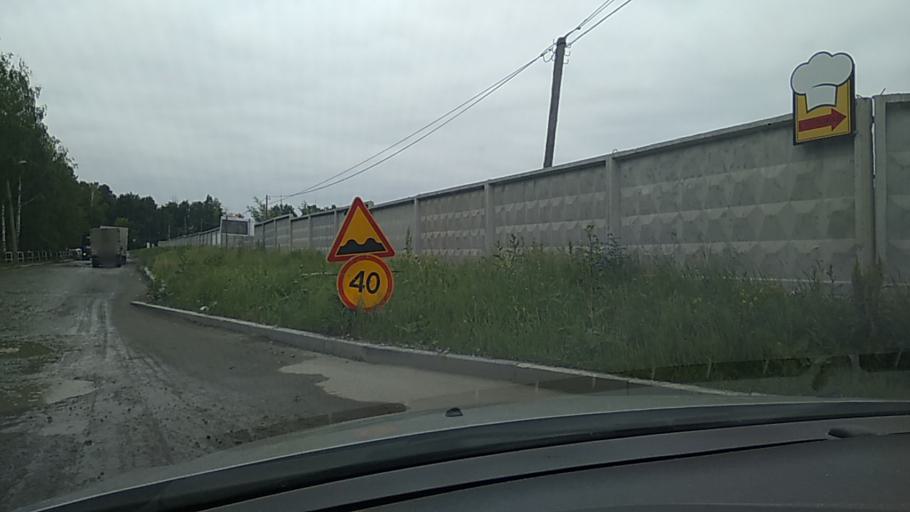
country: RU
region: Sverdlovsk
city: Shuvakish
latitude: 56.8944
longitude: 60.5180
